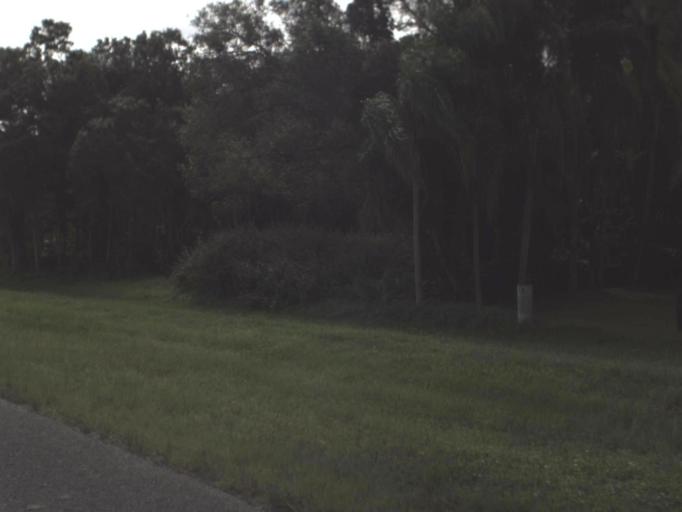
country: US
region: Florida
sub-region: Lee County
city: Olga
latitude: 26.7144
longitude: -81.6680
